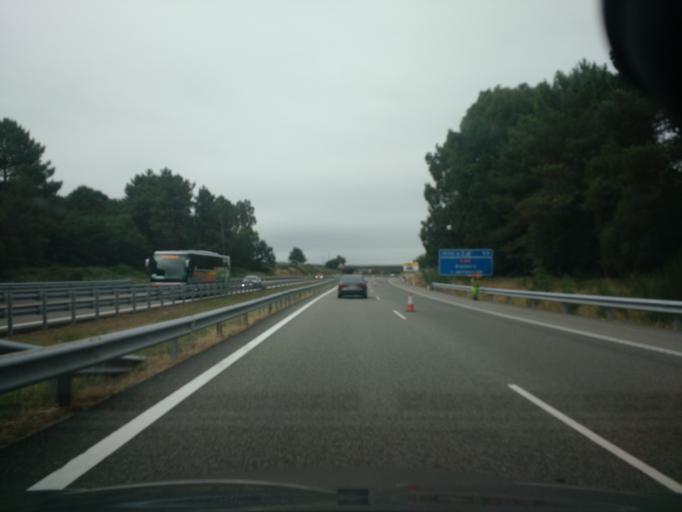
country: ES
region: Galicia
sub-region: Provincia da Coruna
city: Oroso
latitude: 42.9857
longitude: -8.4327
